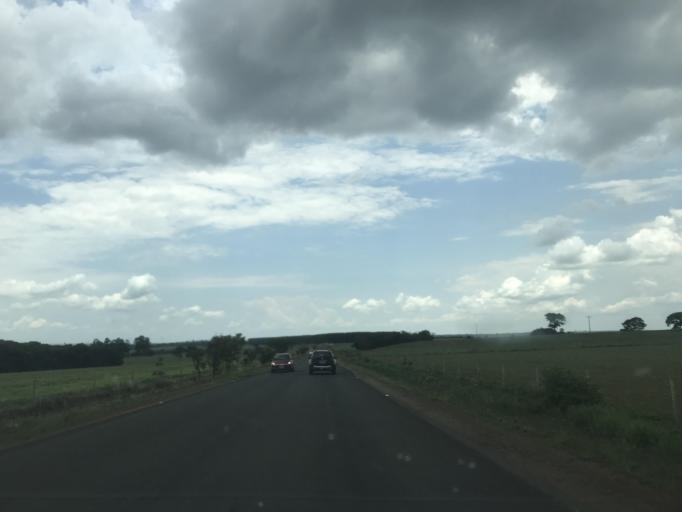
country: BR
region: Goias
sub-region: Vianopolis
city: Vianopolis
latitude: -16.9144
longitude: -48.5546
